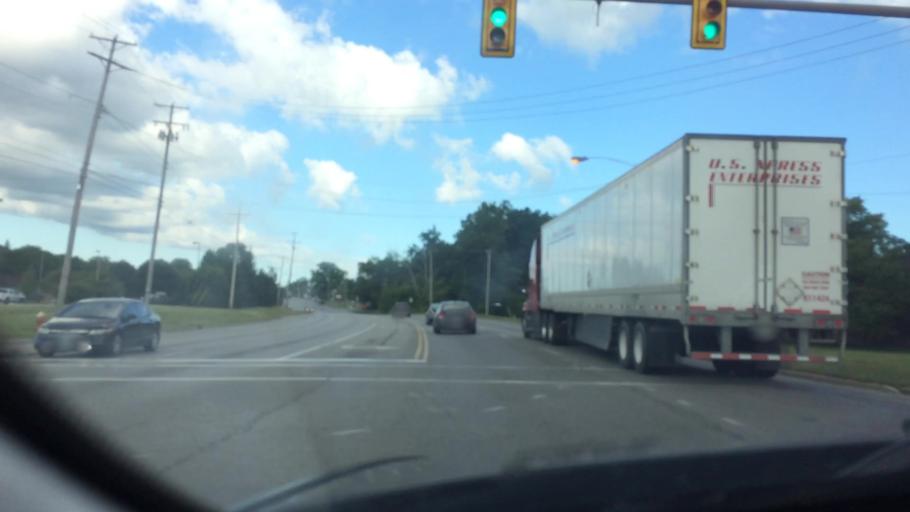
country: US
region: Ohio
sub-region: Lucas County
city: Holland
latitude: 41.6166
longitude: -83.6698
